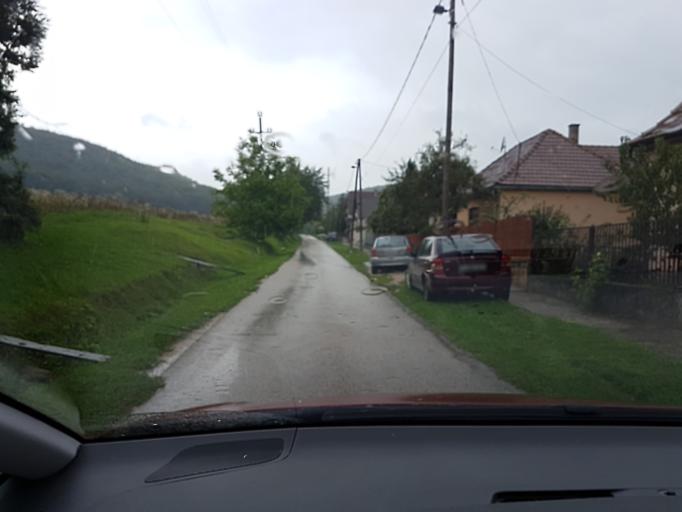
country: HU
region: Komarom-Esztergom
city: Pilismarot
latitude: 47.7804
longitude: 18.8700
